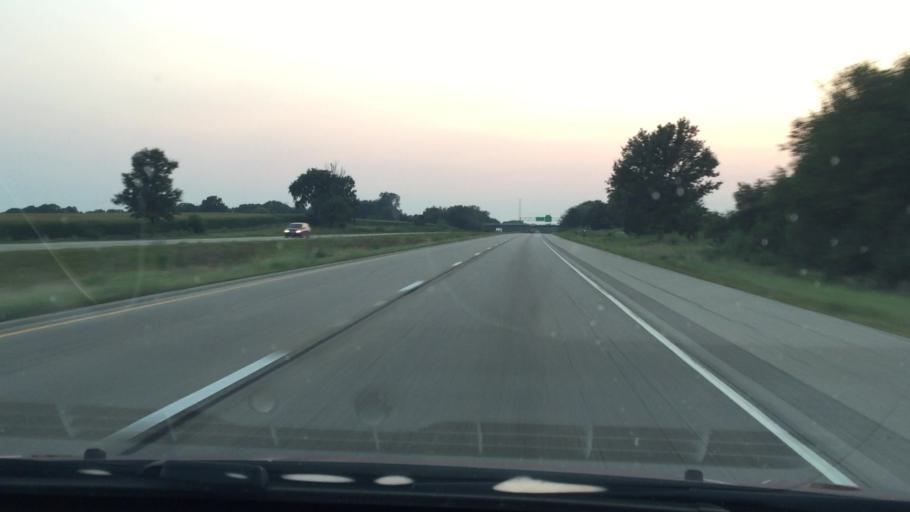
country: US
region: Illinois
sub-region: Bureau County
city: Depue
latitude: 41.4000
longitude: -89.3478
